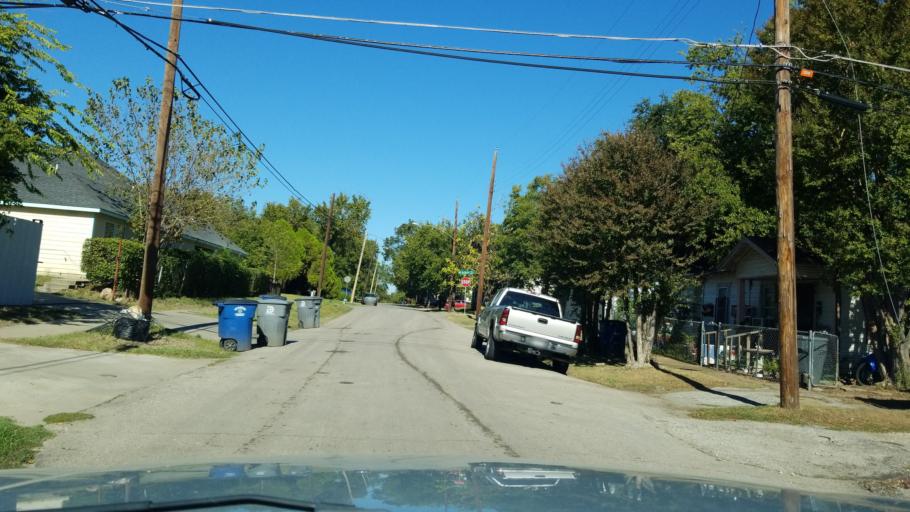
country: US
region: Texas
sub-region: Dallas County
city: Highland Park
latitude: 32.7977
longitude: -96.7465
